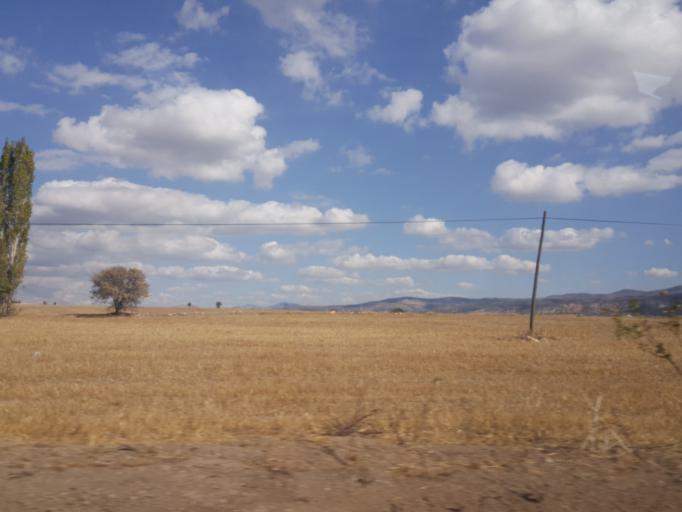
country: TR
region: Tokat
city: Artova
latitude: 40.0494
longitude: 36.3010
